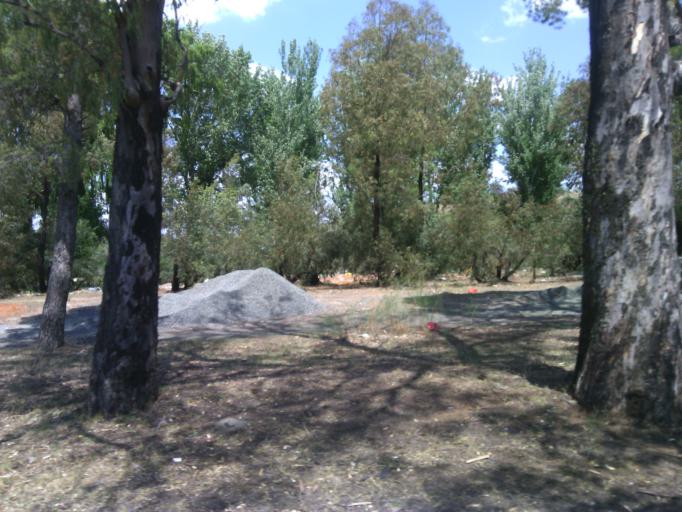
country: ZA
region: Orange Free State
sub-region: Xhariep District Municipality
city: Dewetsdorp
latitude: -29.5821
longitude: 26.6697
